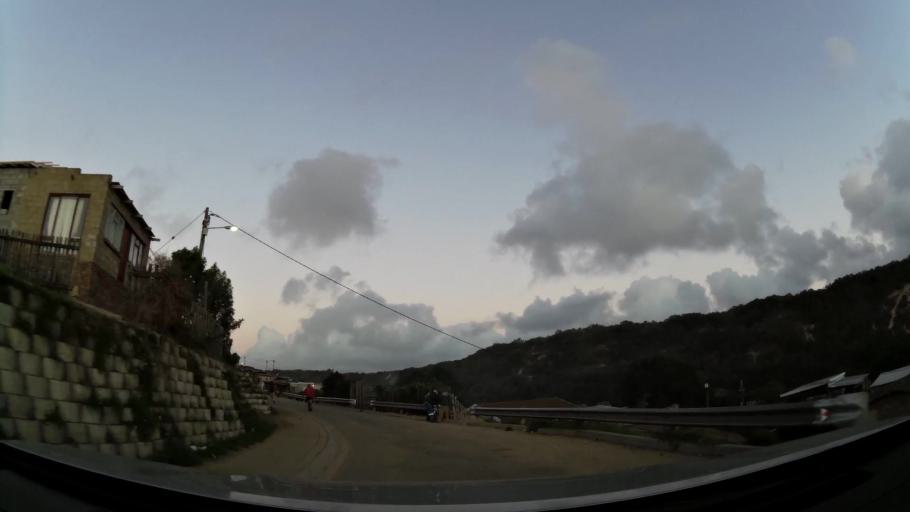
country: ZA
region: Western Cape
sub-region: Eden District Municipality
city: Knysna
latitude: -34.0265
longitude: 22.8204
